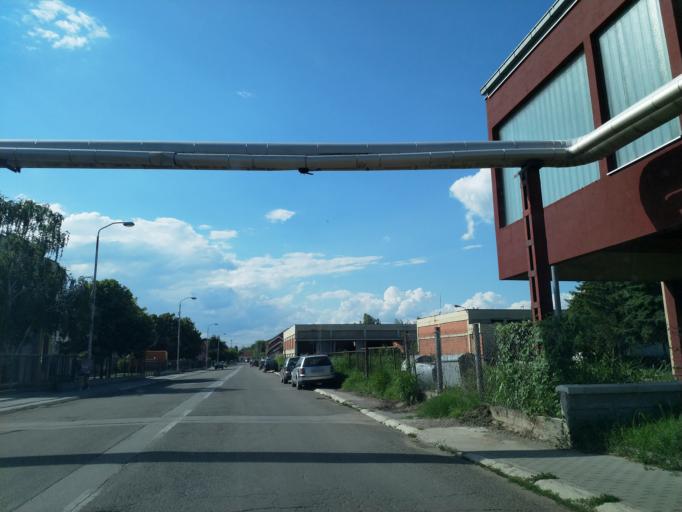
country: RS
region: Central Serbia
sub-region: Pomoravski Okrug
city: Paracin
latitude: 43.8592
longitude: 21.4049
